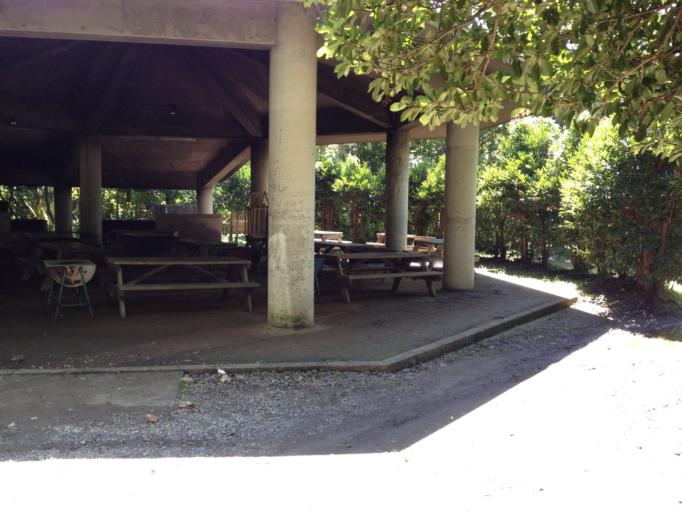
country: JP
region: Wakayama
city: Shingu
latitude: 33.4459
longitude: 135.7820
